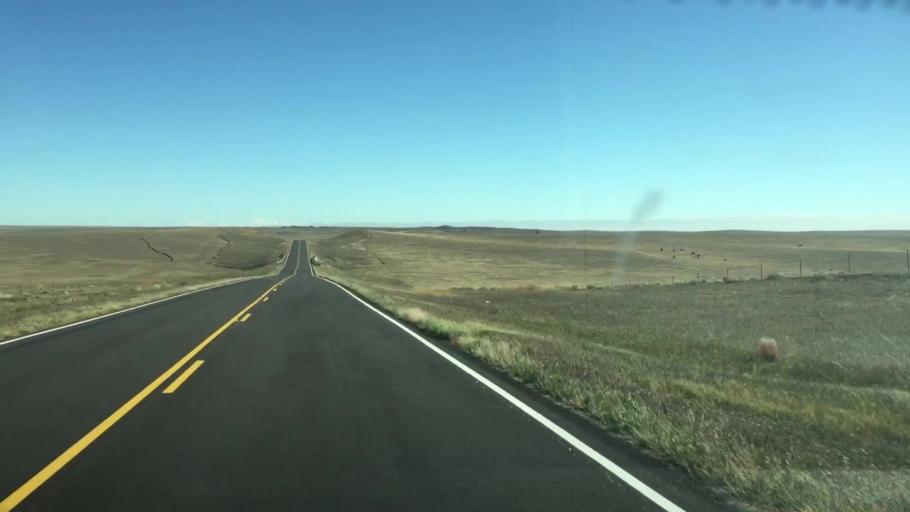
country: US
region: Colorado
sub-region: Lincoln County
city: Limon
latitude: 39.2998
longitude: -103.8502
